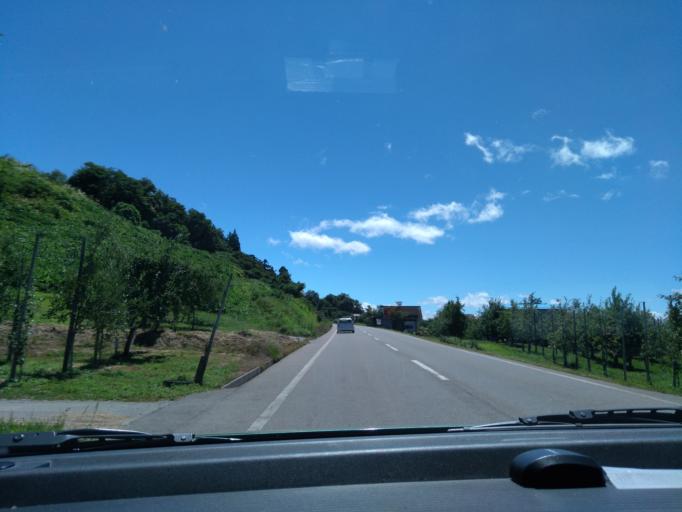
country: JP
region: Akita
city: Yokotemachi
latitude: 39.2305
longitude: 140.5646
